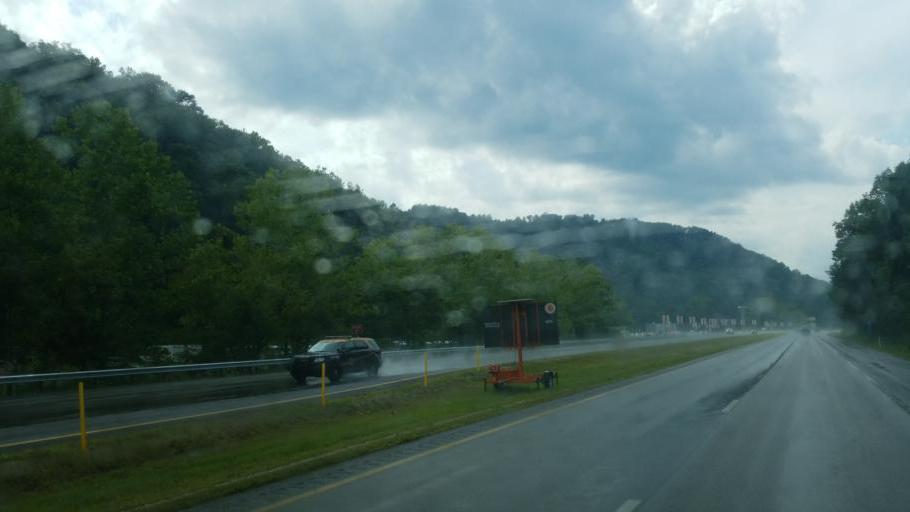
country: US
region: West Virginia
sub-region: Logan County
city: Chapmanville
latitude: 37.9870
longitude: -81.9657
